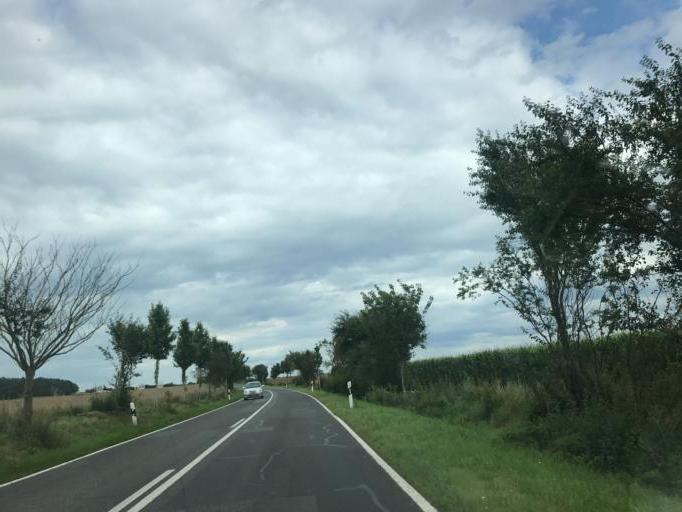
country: DE
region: Mecklenburg-Vorpommern
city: Rechlin
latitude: 53.2316
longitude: 12.7307
